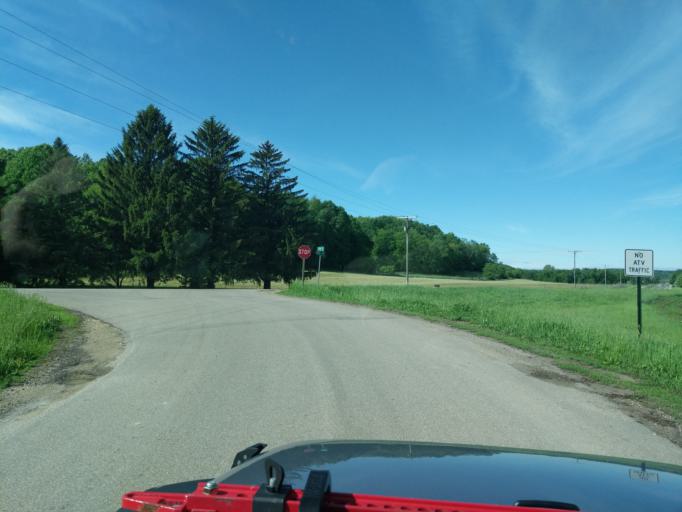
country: US
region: Wisconsin
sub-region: Pierce County
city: River Falls
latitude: 44.8597
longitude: -92.5279
